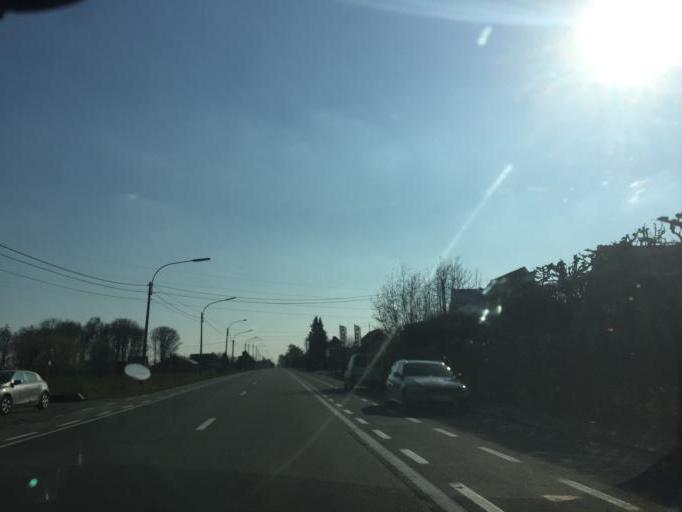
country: BE
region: Flanders
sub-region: Provincie West-Vlaanderen
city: Pittem
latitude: 50.9767
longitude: 3.2415
